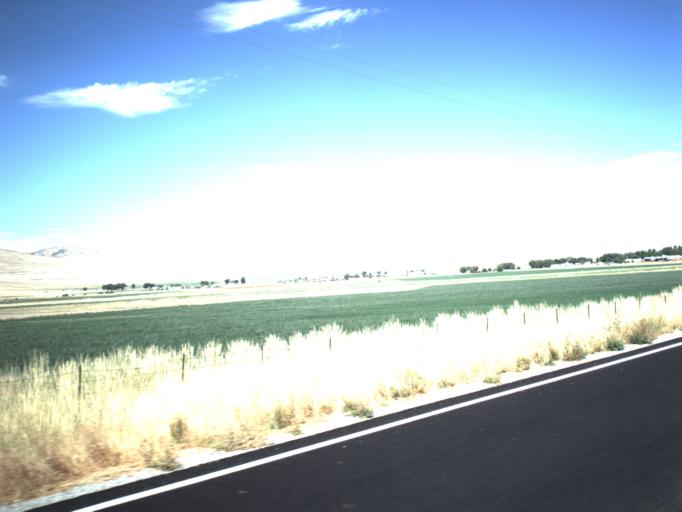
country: US
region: Utah
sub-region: Box Elder County
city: Garland
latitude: 41.7812
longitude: -112.4353
